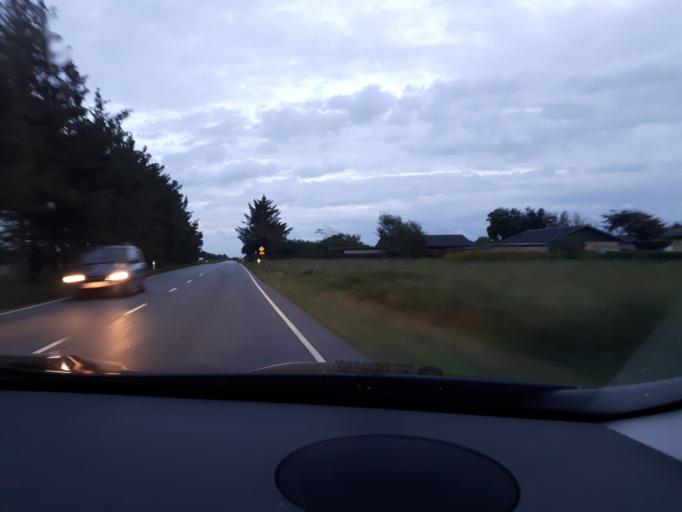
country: DK
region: North Denmark
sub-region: Hjorring Kommune
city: Hirtshals
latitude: 57.5242
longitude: 9.9499
